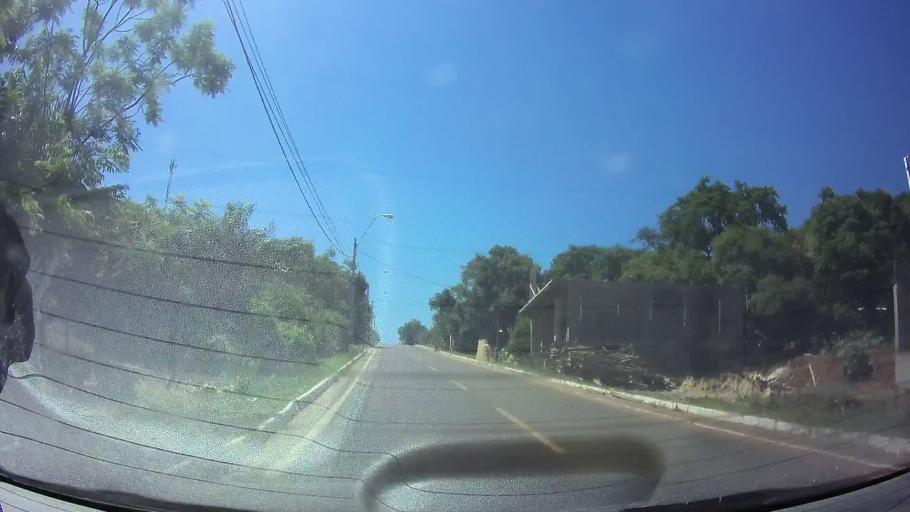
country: PY
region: Central
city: Aregua
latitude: -25.3110
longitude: -57.3945
